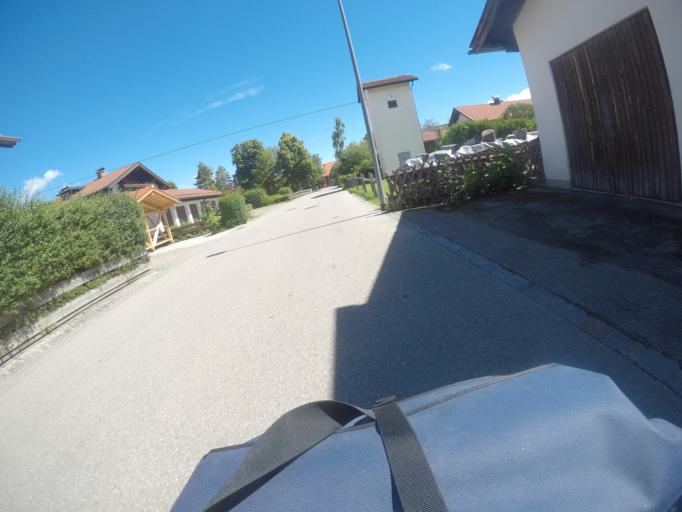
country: DE
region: Bavaria
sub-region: Swabia
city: Schwangau
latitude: 47.5855
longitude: 10.7290
